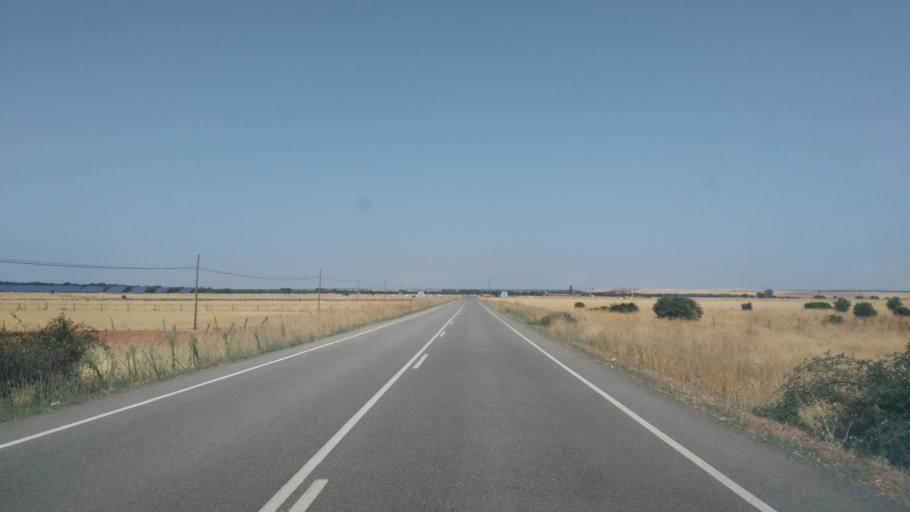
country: ES
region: Castille and Leon
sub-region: Provincia de Salamanca
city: Abusejo
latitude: 40.7135
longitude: -6.1445
